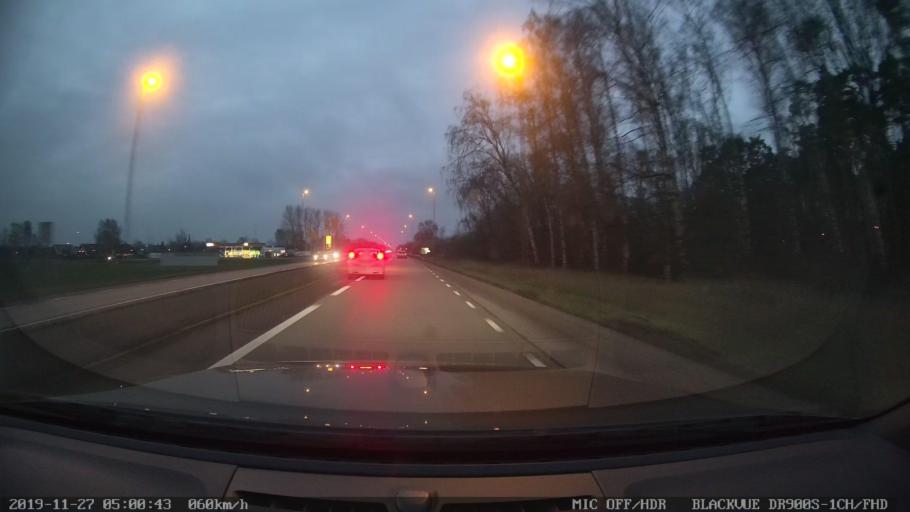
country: SE
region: Skane
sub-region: Hoganas Kommun
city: Hoganas
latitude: 56.1823
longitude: 12.5623
